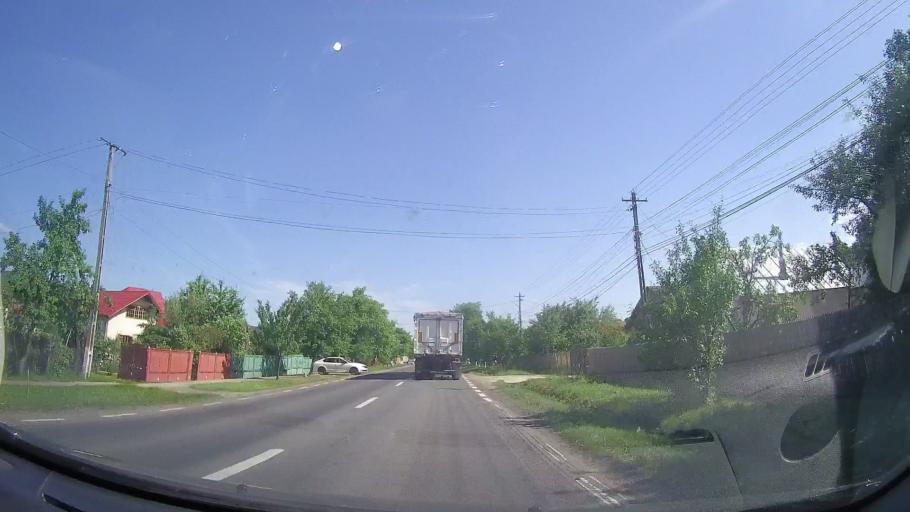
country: RO
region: Prahova
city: Drajna de Jos
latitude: 45.2153
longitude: 26.0372
